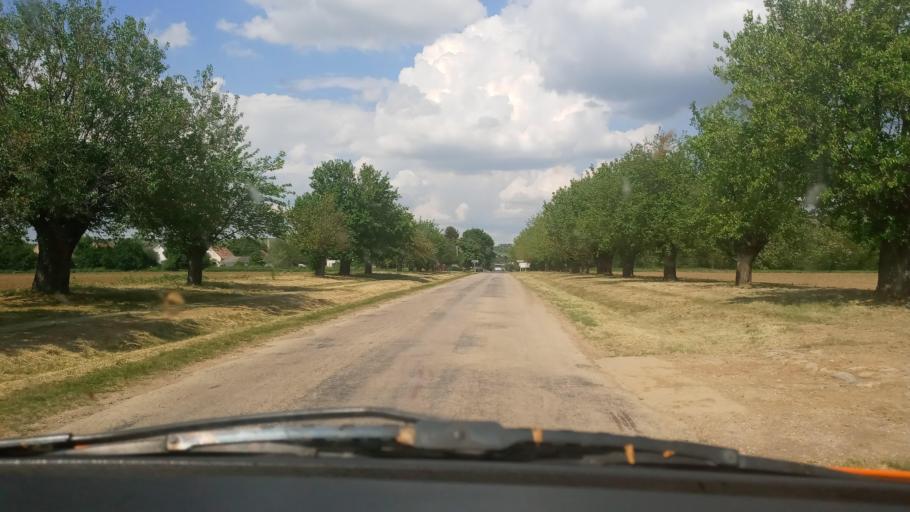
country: HU
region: Baranya
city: Siklos
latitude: 45.8530
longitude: 18.3597
